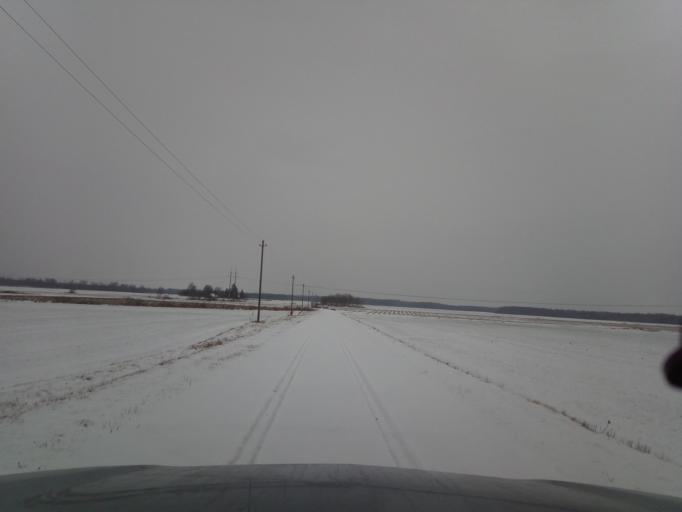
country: LT
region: Panevezys
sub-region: Panevezys City
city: Panevezys
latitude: 55.6279
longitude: 24.3419
